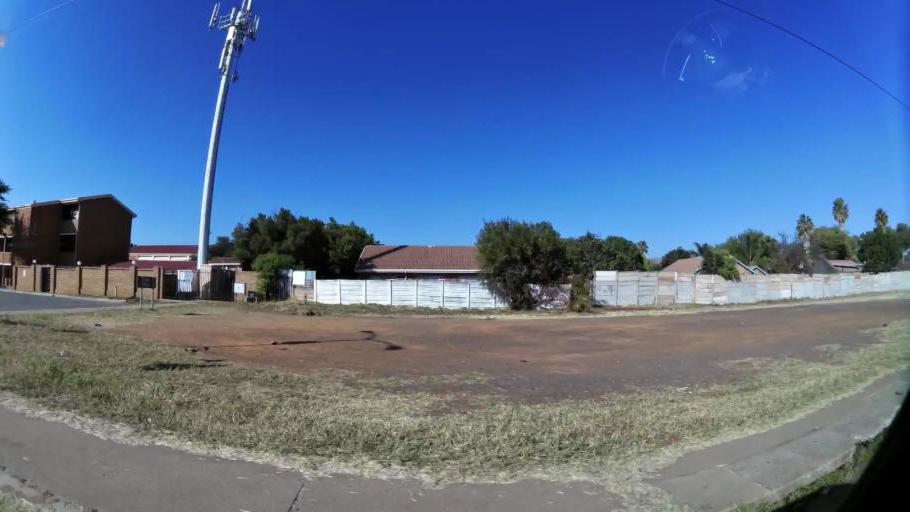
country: ZA
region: Gauteng
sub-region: City of Tshwane Metropolitan Municipality
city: Pretoria
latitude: -25.6664
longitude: 28.1393
